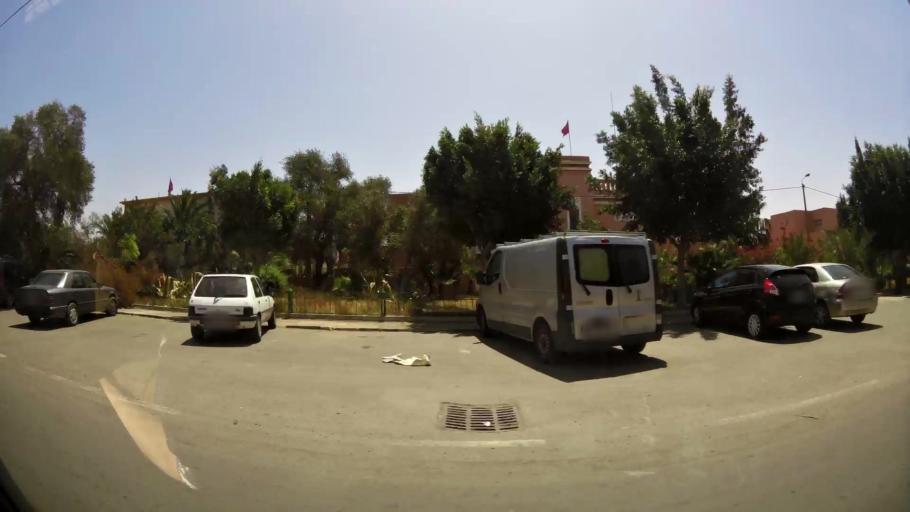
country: MA
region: Souss-Massa-Draa
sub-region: Inezgane-Ait Mellou
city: Inezgane
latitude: 30.3320
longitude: -9.4917
